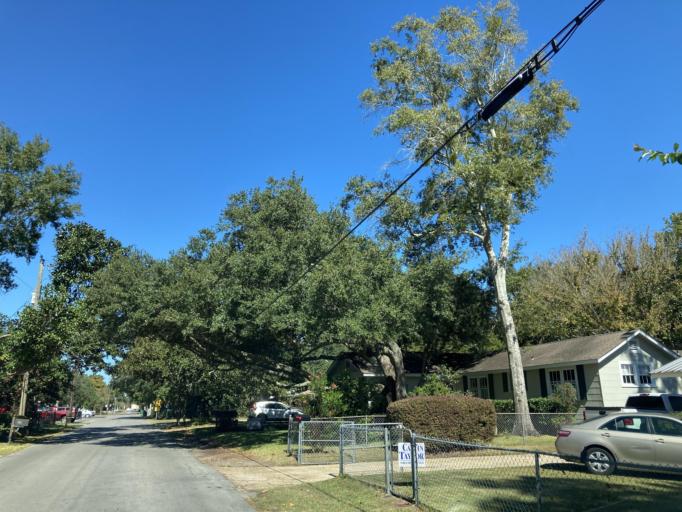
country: US
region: Mississippi
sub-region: Jackson County
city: Ocean Springs
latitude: 30.4096
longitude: -88.8224
